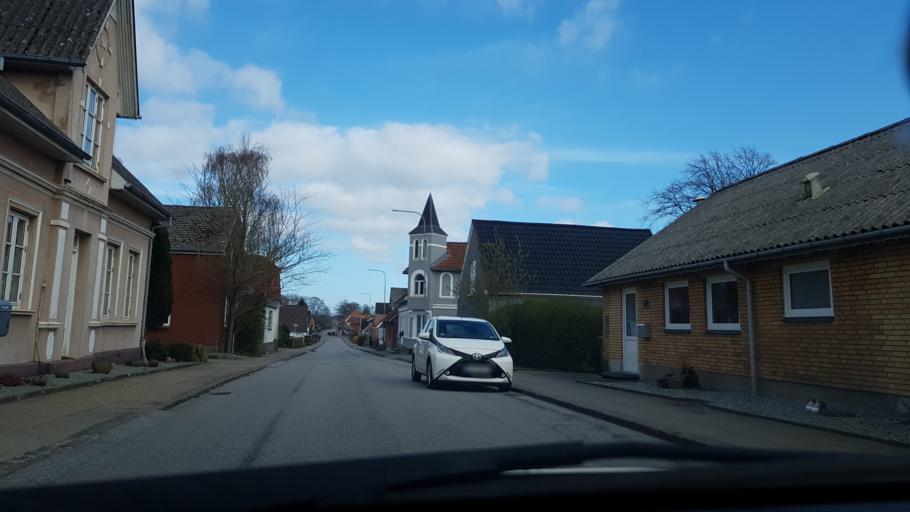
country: DK
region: South Denmark
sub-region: Vejen Kommune
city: Vejen
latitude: 55.4204
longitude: 9.1481
